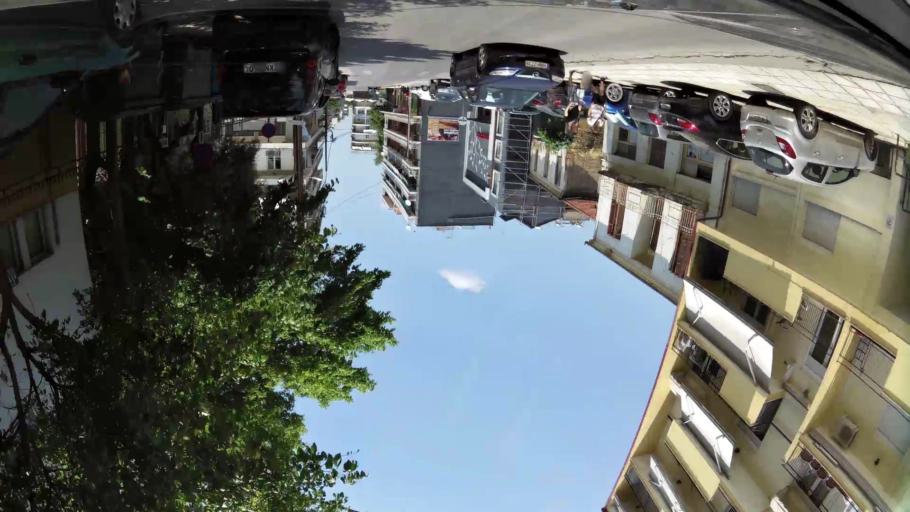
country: GR
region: Central Macedonia
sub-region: Nomos Imathias
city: Veroia
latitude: 40.5192
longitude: 22.1991
